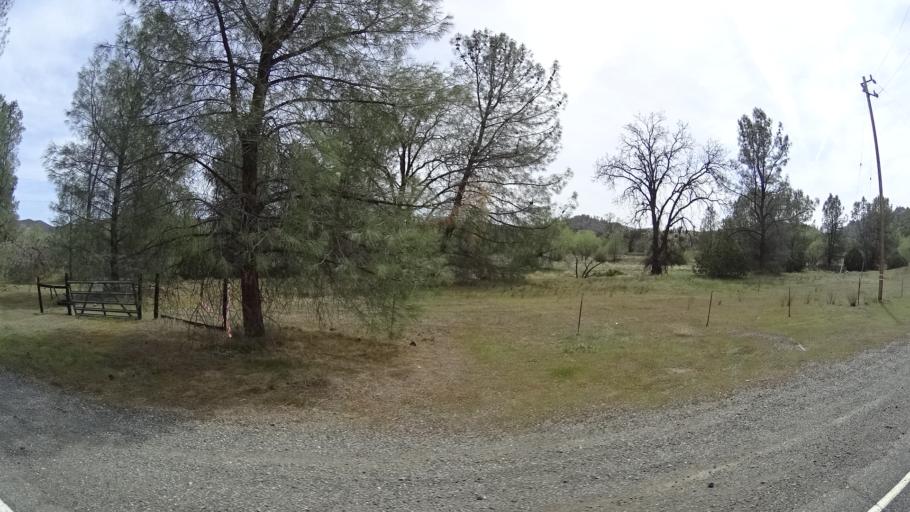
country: US
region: California
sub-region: Glenn County
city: Willows
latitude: 39.4298
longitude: -122.5105
